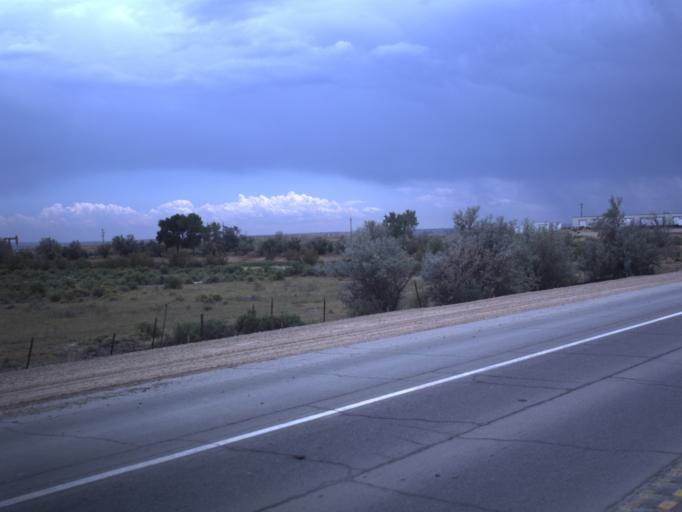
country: US
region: Utah
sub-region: Duchesne County
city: Roosevelt
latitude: 40.2205
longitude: -110.0674
